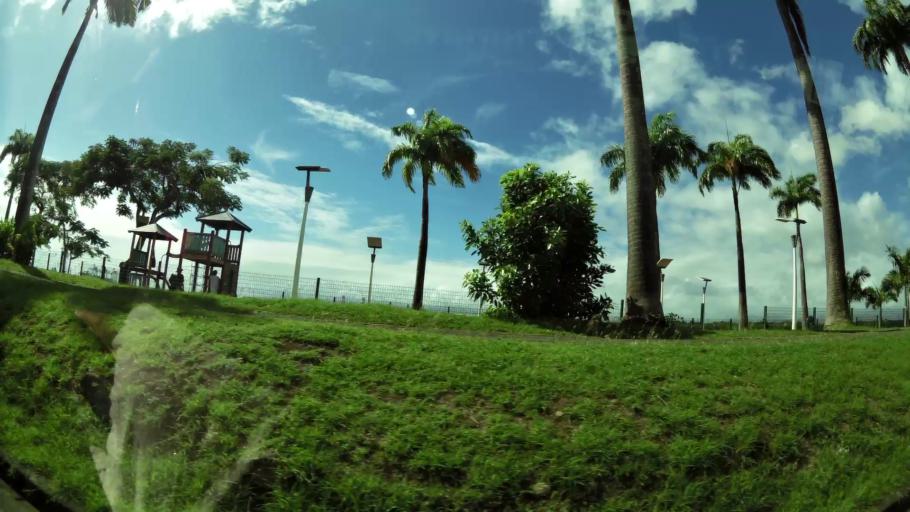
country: GP
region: Guadeloupe
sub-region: Guadeloupe
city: Pointe-a-Pitre
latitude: 16.2475
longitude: -61.5450
